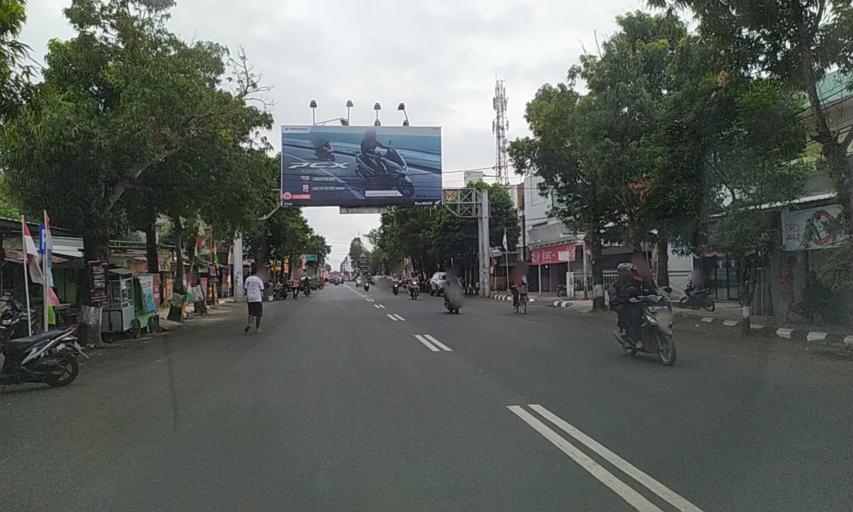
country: ID
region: Central Java
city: Karangbadar Kidul
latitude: -7.7349
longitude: 109.0095
